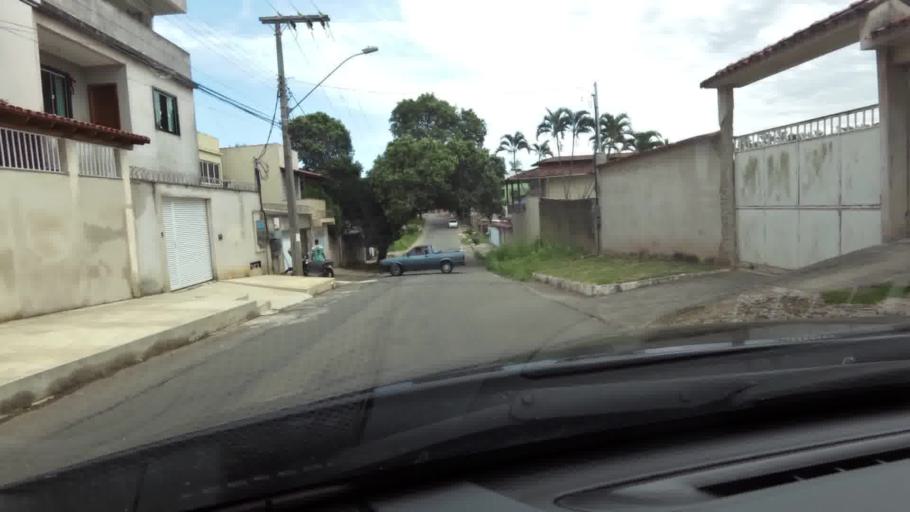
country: BR
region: Espirito Santo
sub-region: Guarapari
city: Guarapari
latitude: -20.6506
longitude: -40.5021
